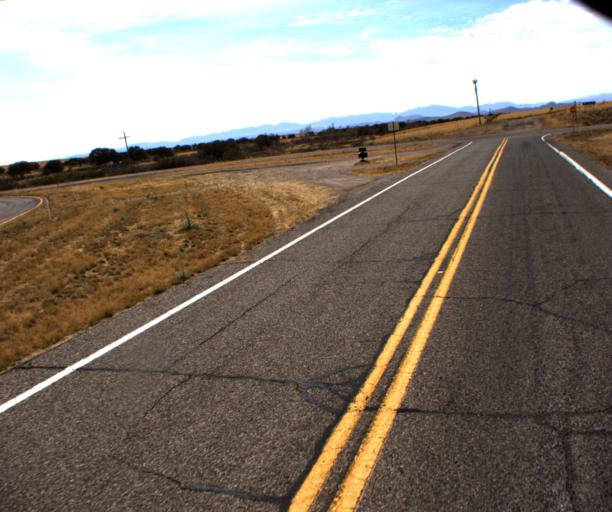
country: US
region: Arizona
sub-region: Cochise County
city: Willcox
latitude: 32.0068
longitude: -109.4391
